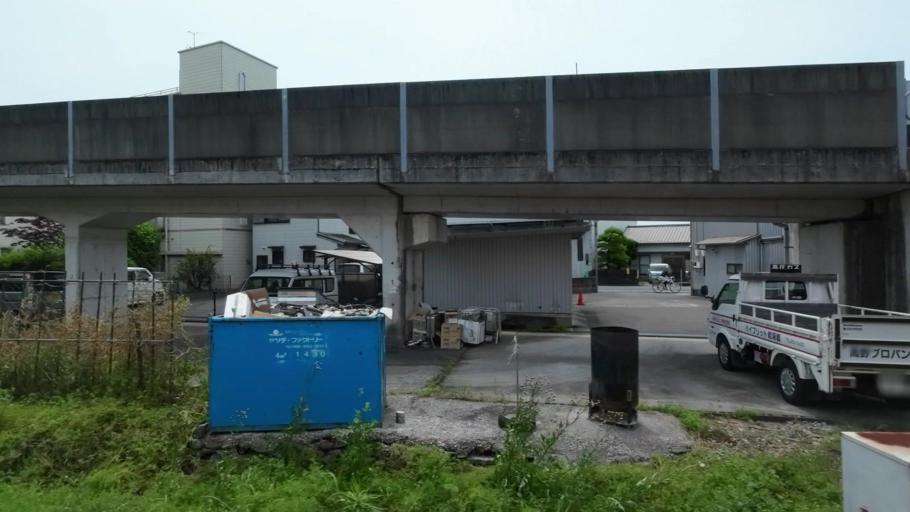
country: JP
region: Kochi
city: Kochi-shi
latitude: 33.5800
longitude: 133.6473
